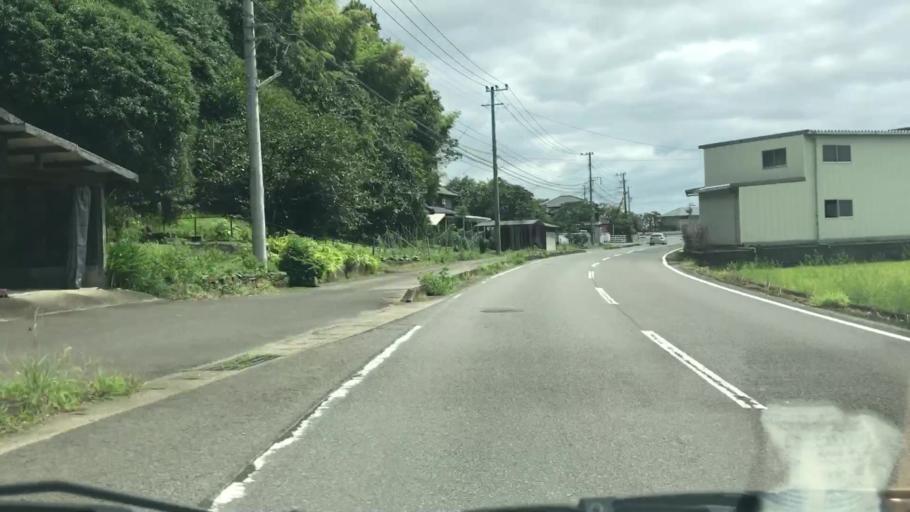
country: JP
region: Saga Prefecture
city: Takeocho-takeo
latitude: 33.2291
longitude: 130.1530
